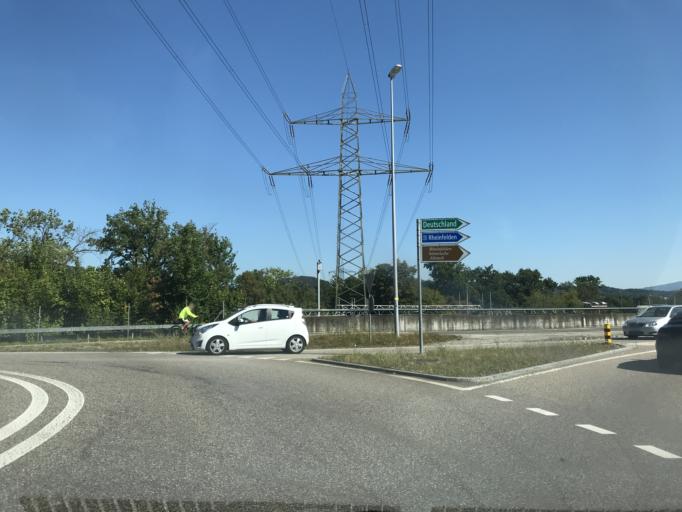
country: CH
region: Aargau
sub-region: Bezirk Rheinfelden
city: Kaiseraugst
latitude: 47.5451
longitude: 7.7568
